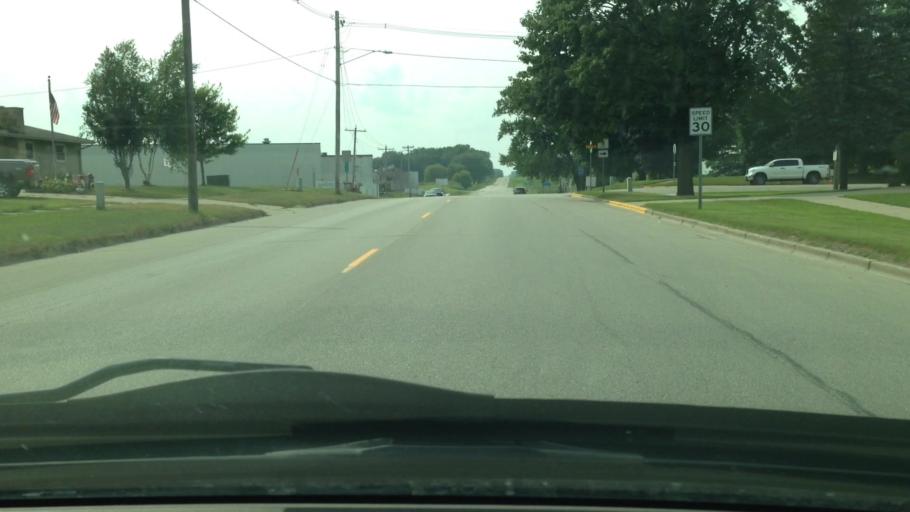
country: US
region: Minnesota
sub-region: Wabasha County
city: Plainview
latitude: 44.1650
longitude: -92.1787
